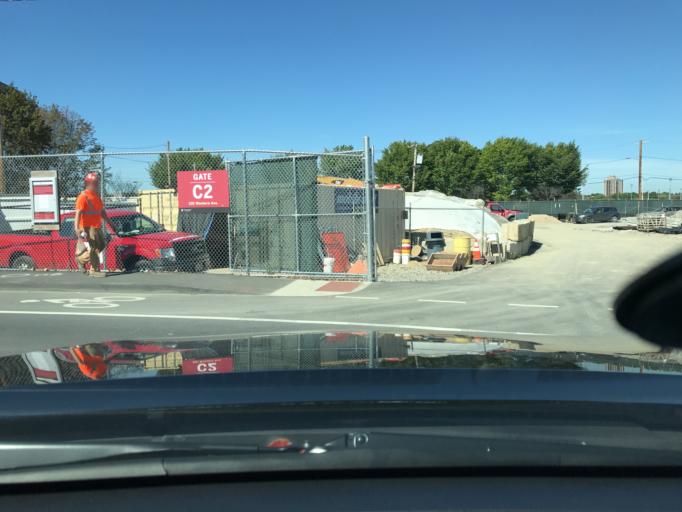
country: US
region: Massachusetts
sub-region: Middlesex County
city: Cambridge
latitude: 42.3635
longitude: -71.1280
